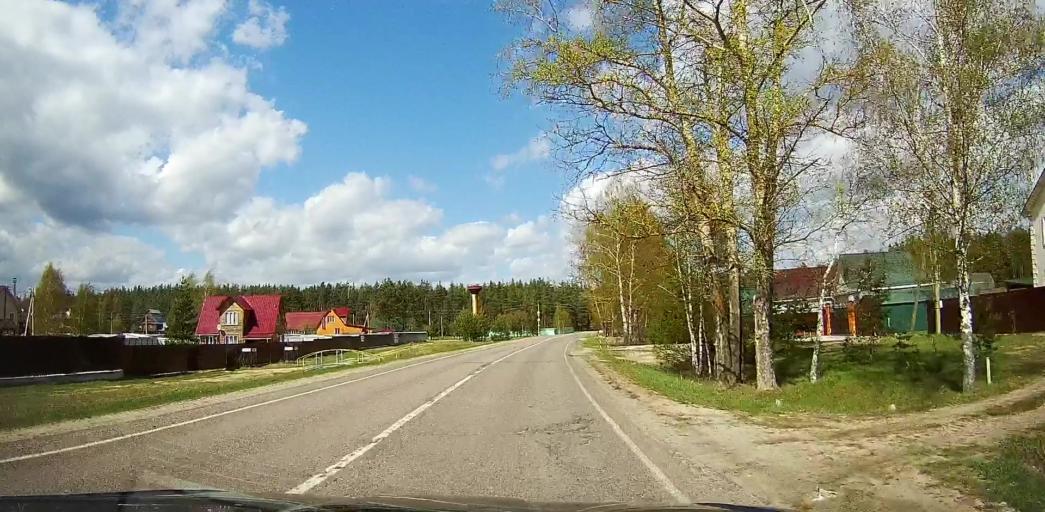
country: RU
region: Moskovskaya
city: Davydovo
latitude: 55.5608
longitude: 38.8130
